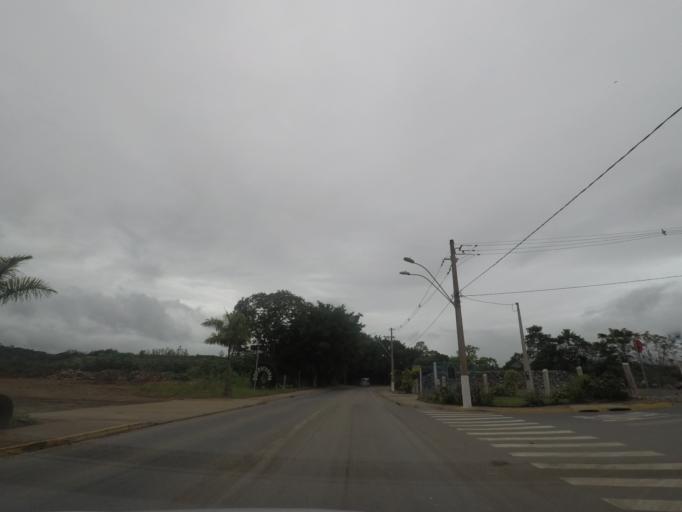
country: BR
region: Sao Paulo
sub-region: Cajati
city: Cajati
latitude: -24.7242
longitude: -48.0988
